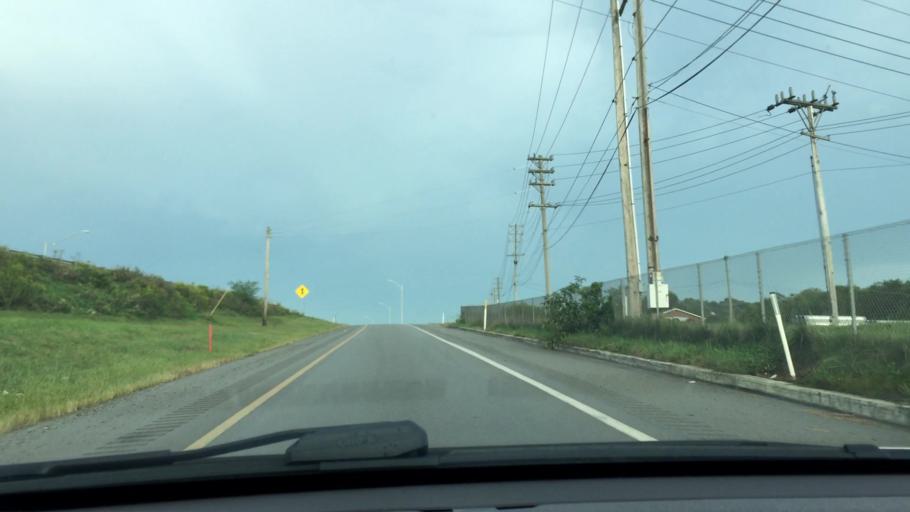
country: US
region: Pennsylvania
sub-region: Washington County
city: East Washington
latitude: 40.1553
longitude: -80.1304
